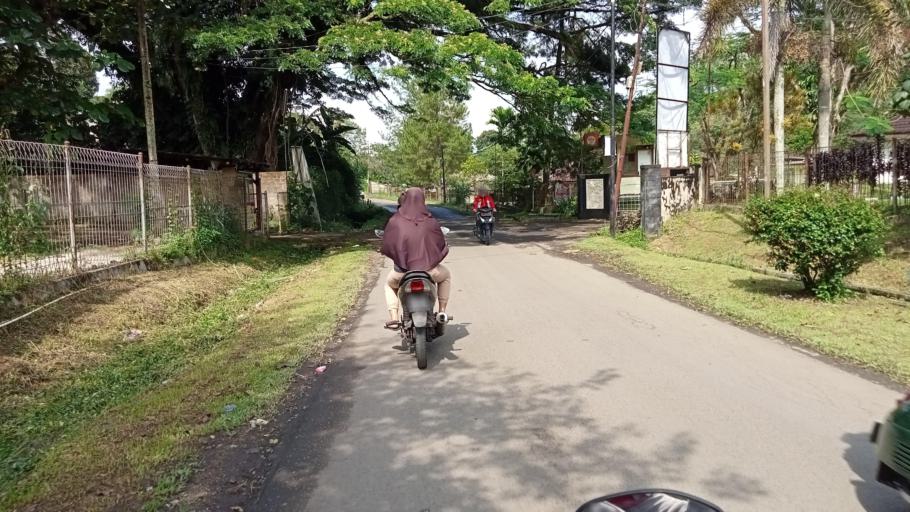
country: ID
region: West Java
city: Caringin
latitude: -6.6470
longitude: 106.9095
